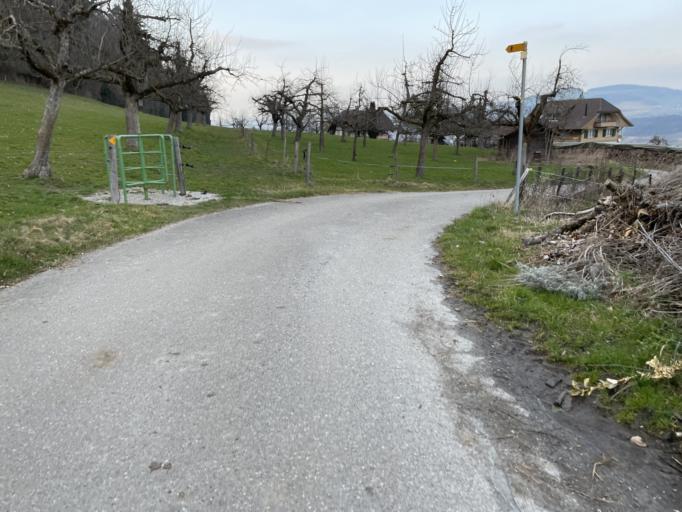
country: CH
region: Bern
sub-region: Bern-Mittelland District
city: Munsingen
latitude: 46.8472
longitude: 7.5477
